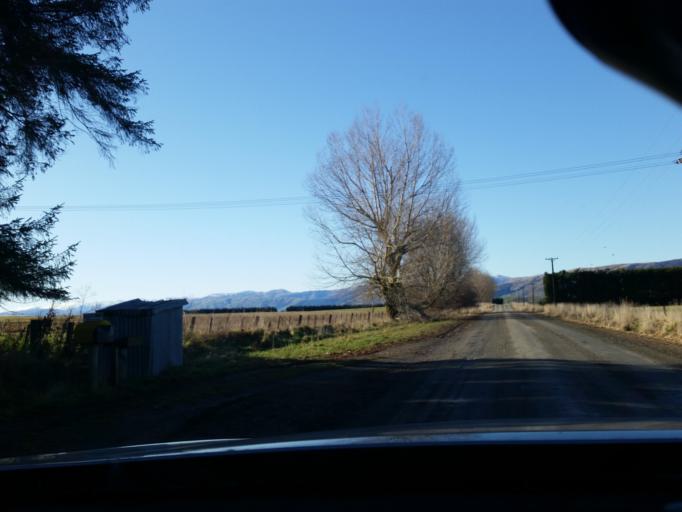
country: NZ
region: Otago
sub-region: Queenstown-Lakes District
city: Kingston
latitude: -45.7463
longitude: 168.7288
